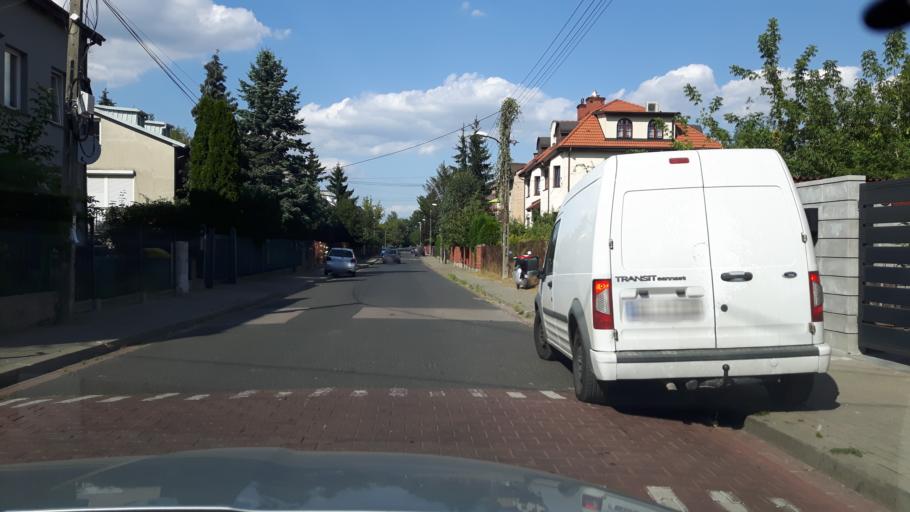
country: PL
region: Masovian Voivodeship
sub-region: Warszawa
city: Wlochy
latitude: 52.2045
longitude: 20.9281
